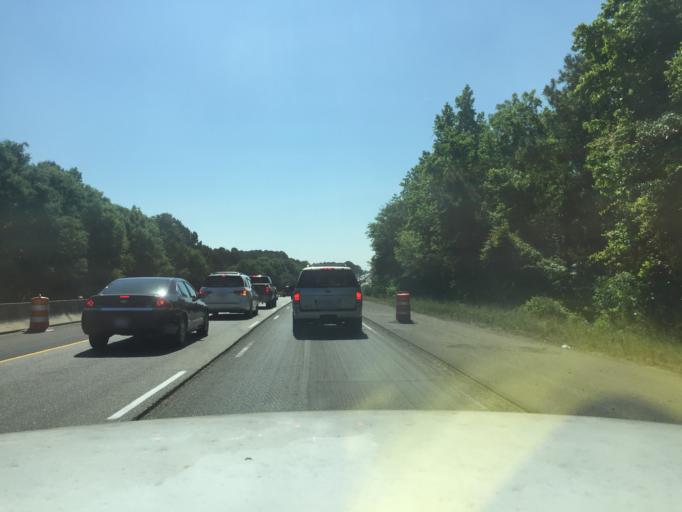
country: US
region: Georgia
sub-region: Chatham County
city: Georgetown
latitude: 31.9931
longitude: -81.2316
